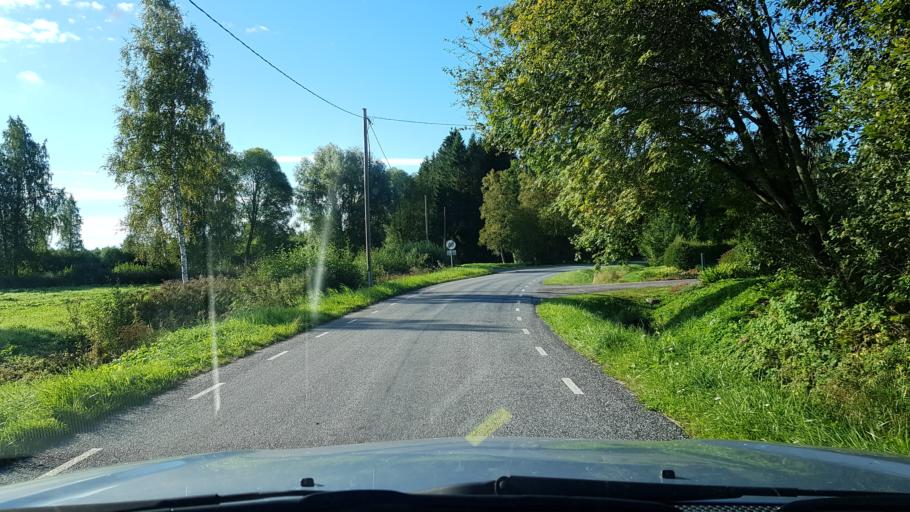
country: EE
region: Harju
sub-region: Rae vald
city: Vaida
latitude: 59.3040
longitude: 24.9271
